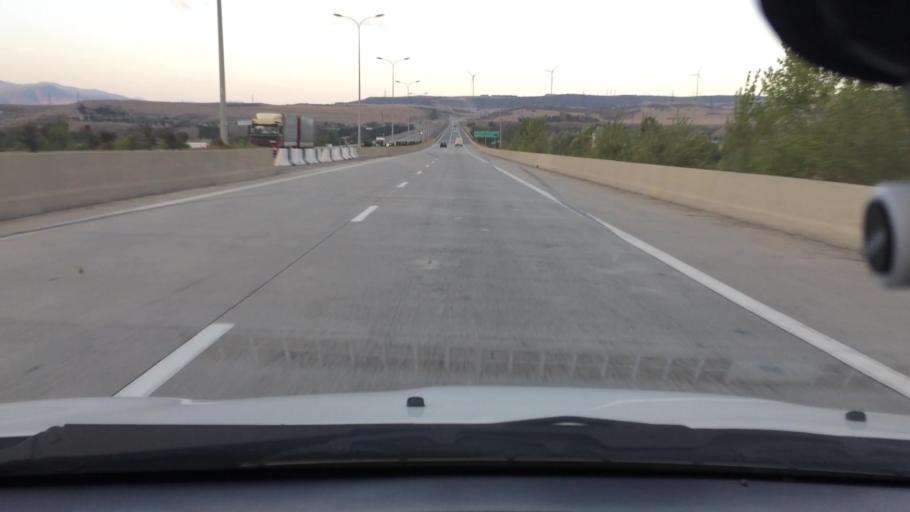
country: GE
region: Shida Kartli
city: Gori
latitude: 42.0175
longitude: 44.0931
